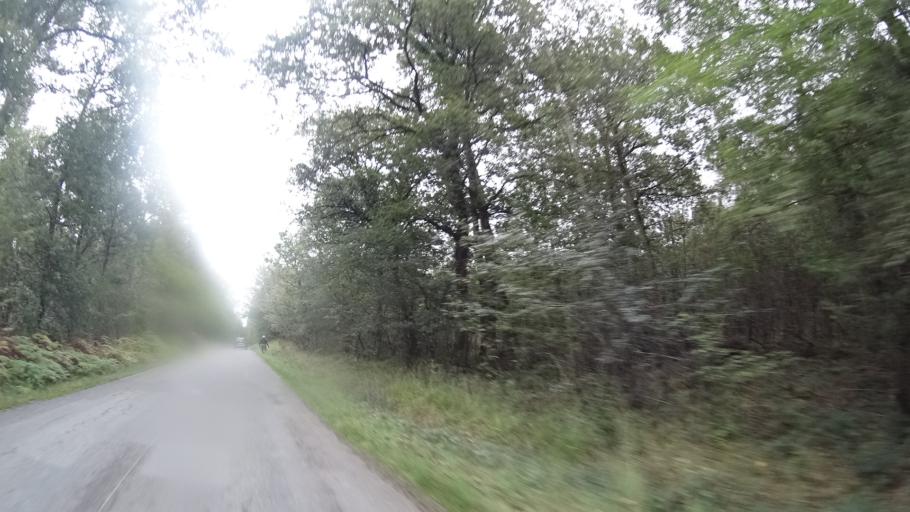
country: FR
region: Brittany
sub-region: Departement d'Ille-et-Vilaine
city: Paimpont
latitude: 48.0766
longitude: -2.1588
